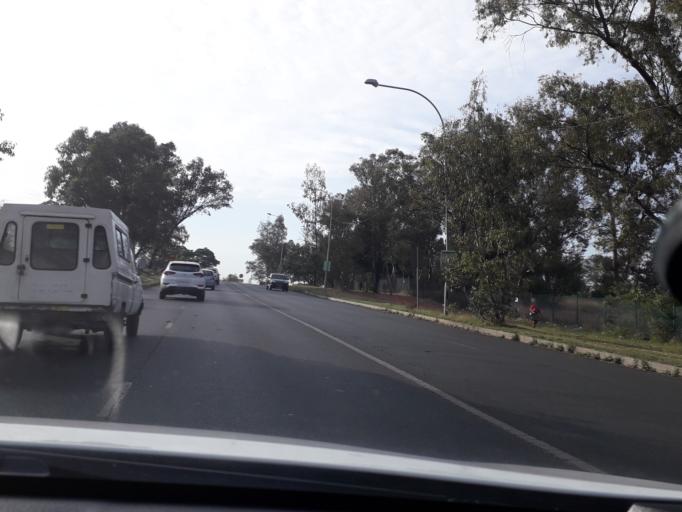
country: ZA
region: Gauteng
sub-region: City of Johannesburg Metropolitan Municipality
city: Modderfontein
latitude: -26.1434
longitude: 28.1223
